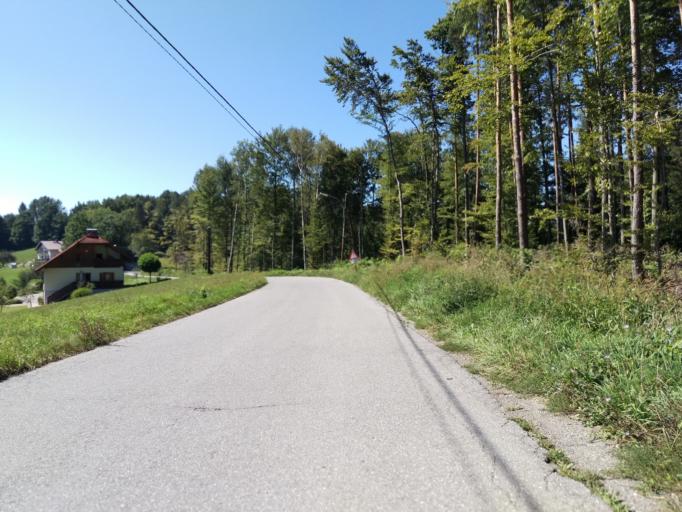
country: AT
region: Styria
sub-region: Politischer Bezirk Graz-Umgebung
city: Hart bei Graz
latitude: 47.0716
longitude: 15.5305
